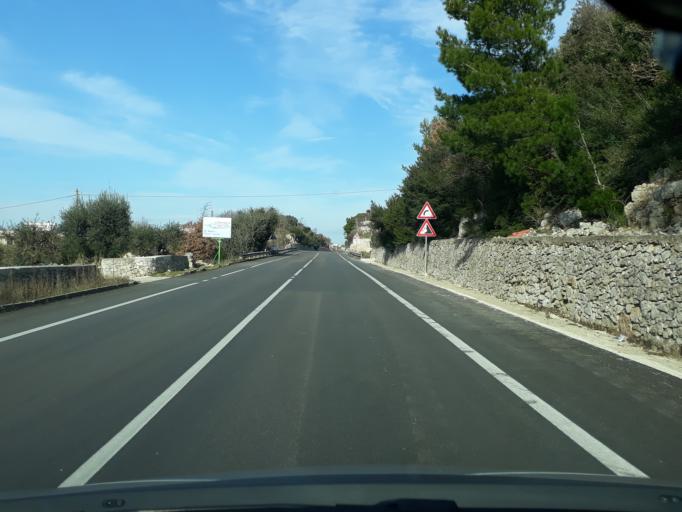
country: IT
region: Apulia
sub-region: Provincia di Bari
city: Locorotondo
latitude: 40.7813
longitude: 17.3389
